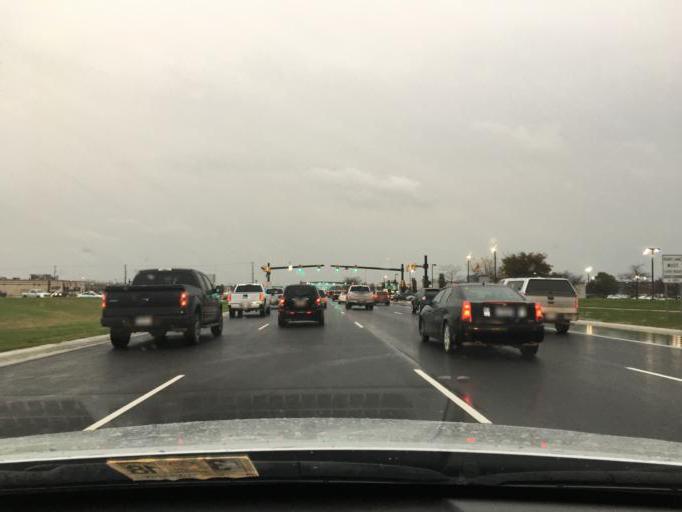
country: US
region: Michigan
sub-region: Macomb County
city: Utica
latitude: 42.6267
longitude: -82.9968
